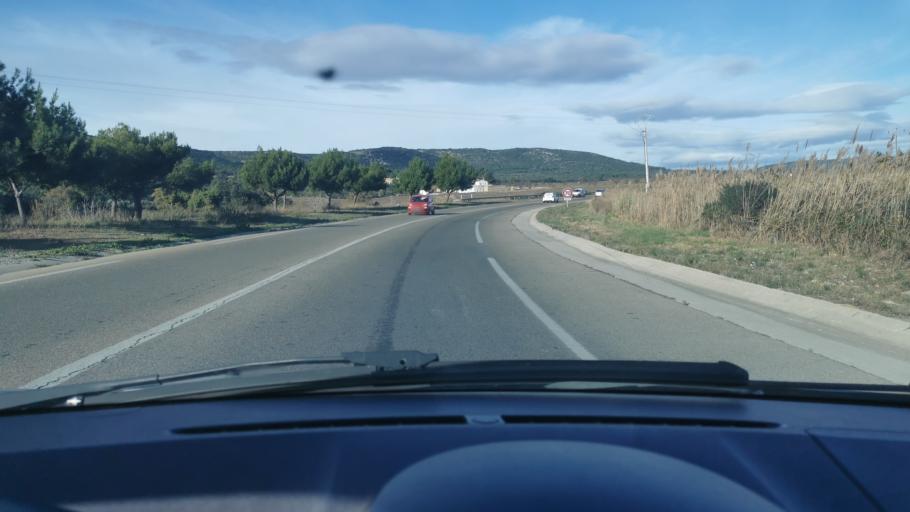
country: FR
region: Languedoc-Roussillon
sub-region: Departement de l'Herault
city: Frontignan
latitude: 43.4672
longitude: 3.7662
